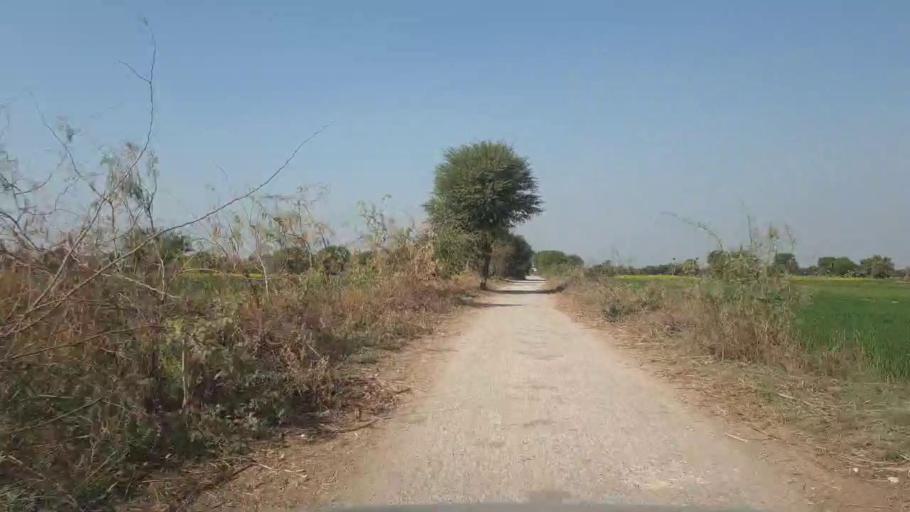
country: PK
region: Sindh
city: Chambar
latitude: 25.3059
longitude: 68.8457
